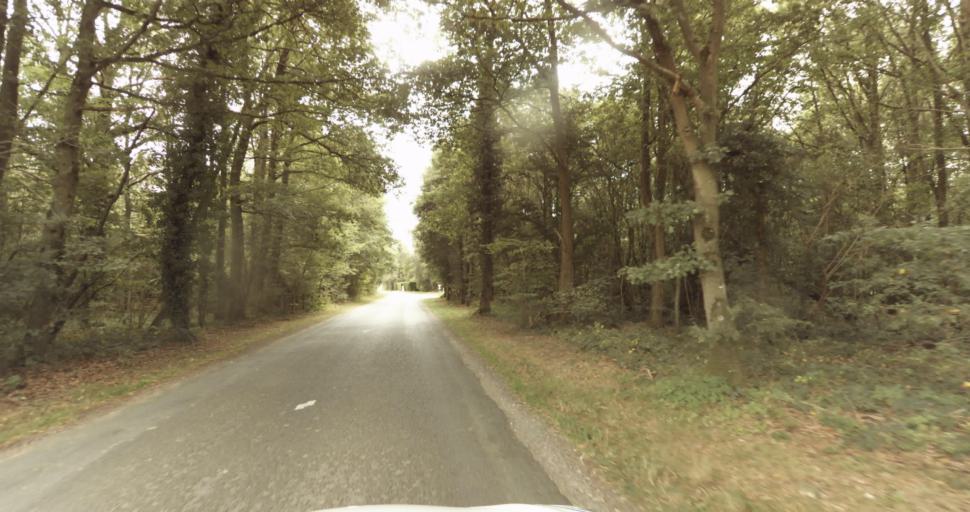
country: FR
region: Haute-Normandie
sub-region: Departement de l'Eure
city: Saint-Germain-sur-Avre
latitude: 48.8015
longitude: 1.2745
